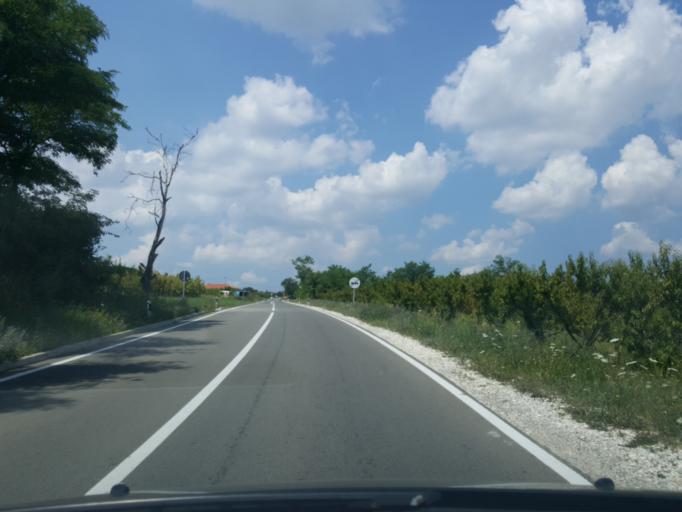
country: RS
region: Central Serbia
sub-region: Sumadijski Okrug
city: Topola
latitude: 44.2278
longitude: 20.6463
